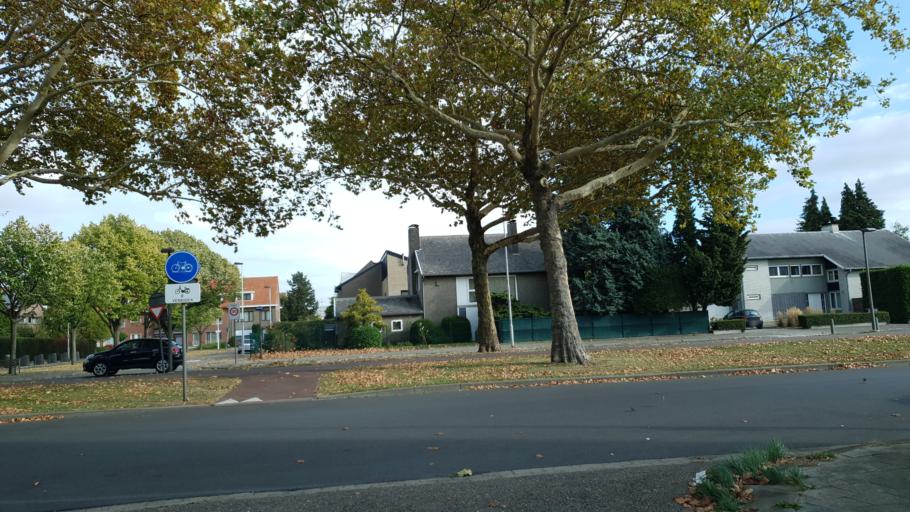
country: BE
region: Flanders
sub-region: Provincie Antwerpen
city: Antwerpen
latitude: 51.2316
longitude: 4.3861
